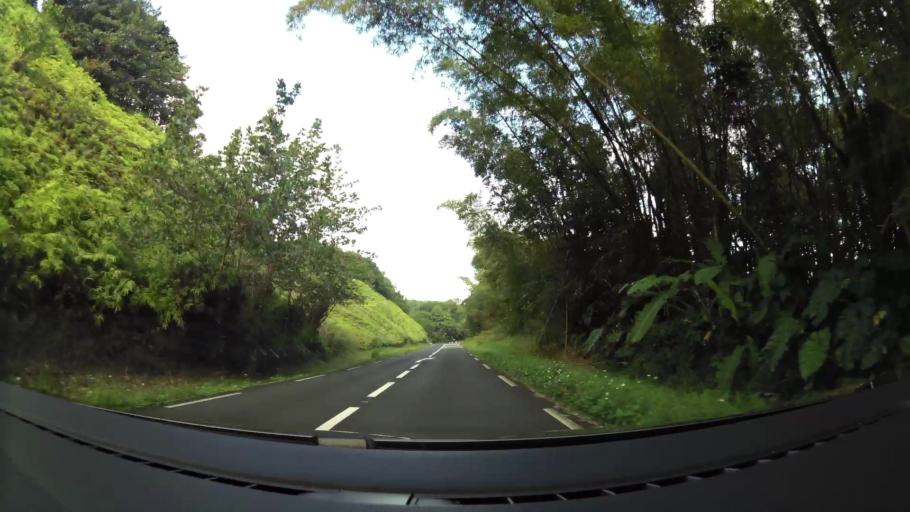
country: GP
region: Guadeloupe
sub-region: Guadeloupe
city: Bouillante
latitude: 16.1788
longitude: -61.7177
